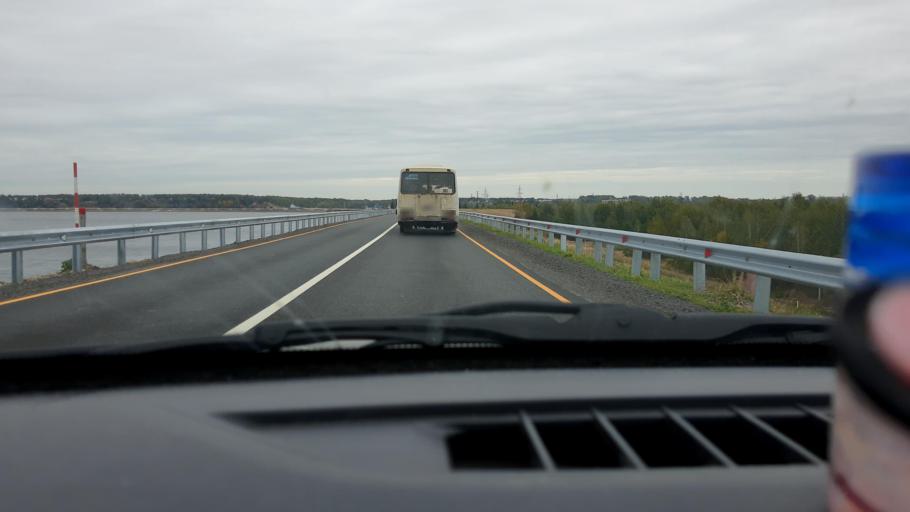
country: RU
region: Nizjnij Novgorod
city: Zavolzh'ye
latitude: 56.6710
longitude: 43.4018
